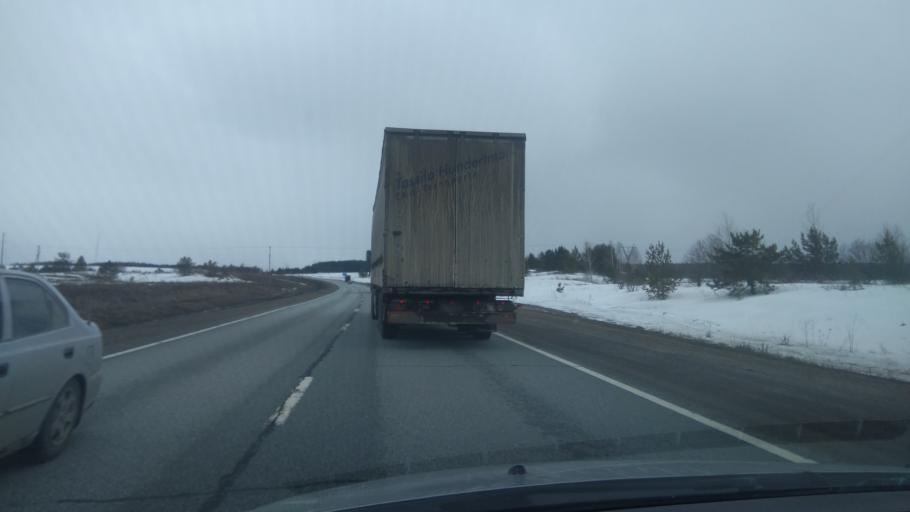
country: RU
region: Sverdlovsk
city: Achit
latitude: 56.8870
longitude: 57.6142
